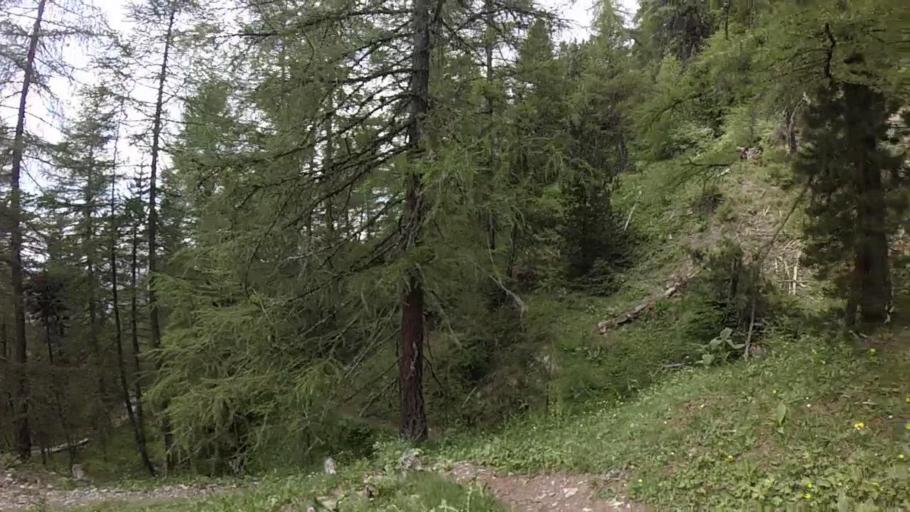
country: FR
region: Provence-Alpes-Cote d'Azur
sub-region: Departement des Alpes-de-Haute-Provence
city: Seyne-les-Alpes
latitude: 44.4063
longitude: 6.3704
